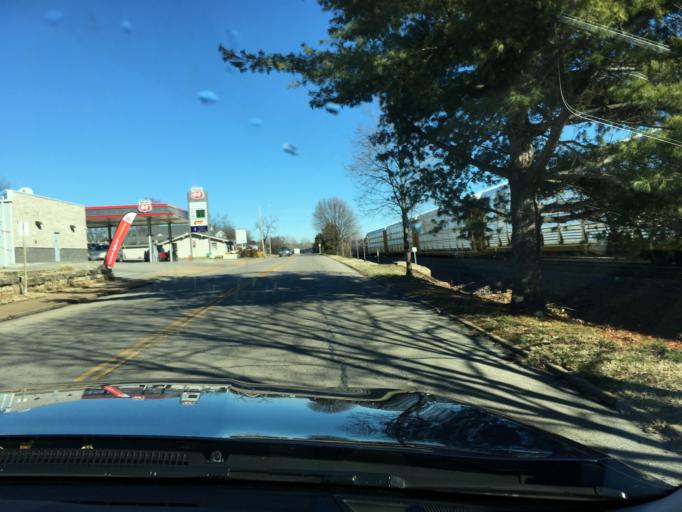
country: US
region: Missouri
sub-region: Jefferson County
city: De Soto
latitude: 38.1441
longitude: -90.5517
